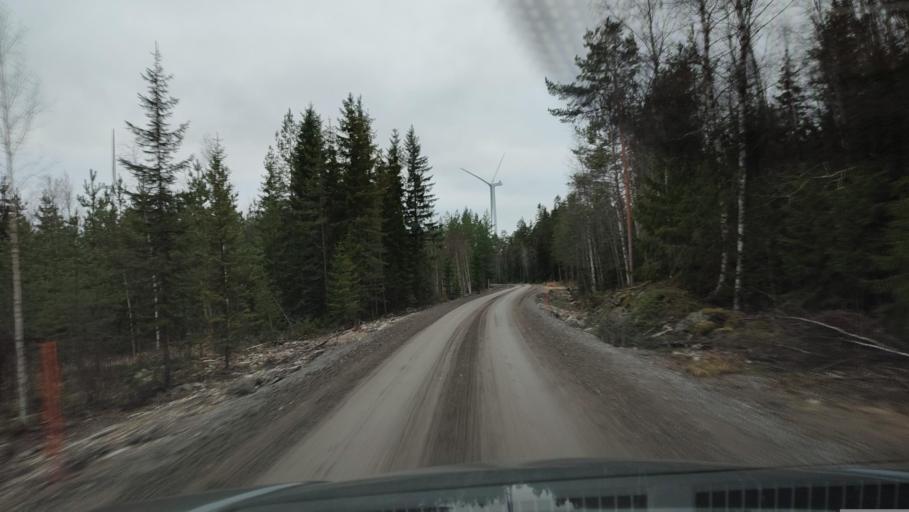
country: FI
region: Southern Ostrobothnia
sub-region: Suupohja
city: Karijoki
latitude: 62.1979
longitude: 21.5900
